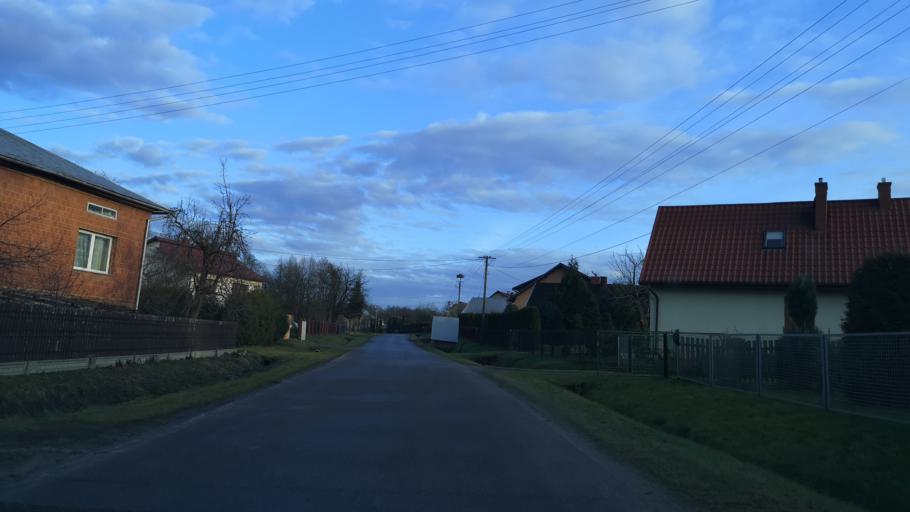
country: PL
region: Subcarpathian Voivodeship
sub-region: Powiat przeworski
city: Sieniawa
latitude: 50.2536
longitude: 22.6169
